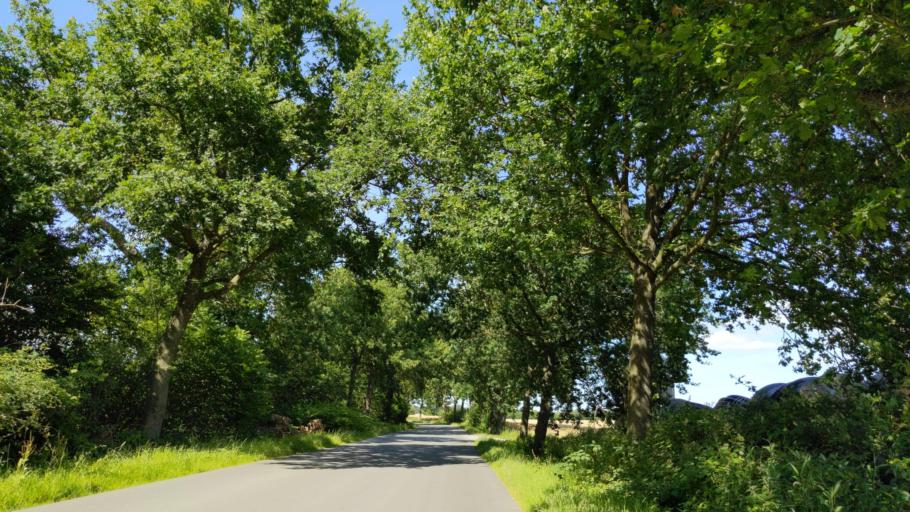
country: DE
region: Schleswig-Holstein
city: Neustadt in Holstein
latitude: 54.1327
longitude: 10.7740
